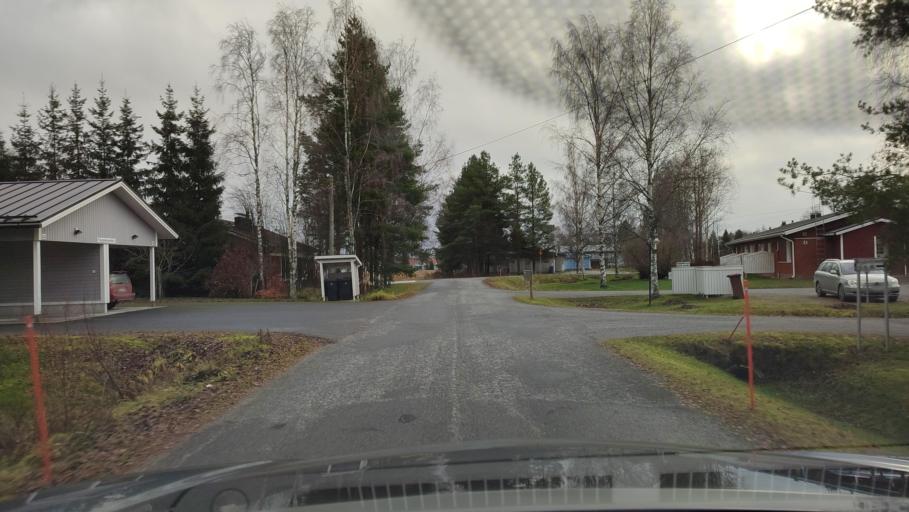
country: FI
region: Southern Ostrobothnia
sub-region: Suupohja
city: Kauhajoki
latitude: 62.4154
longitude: 22.1784
